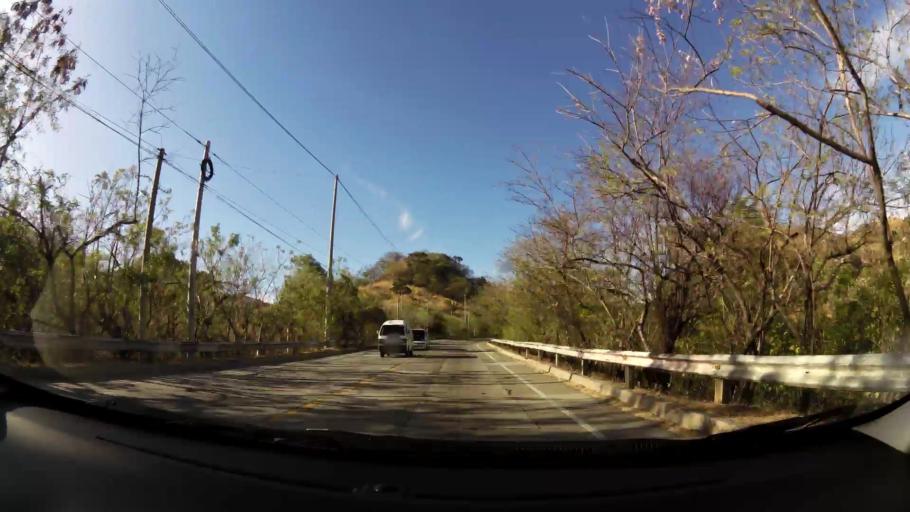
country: SV
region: Santa Ana
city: Texistepeque
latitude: 14.1434
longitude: -89.5139
